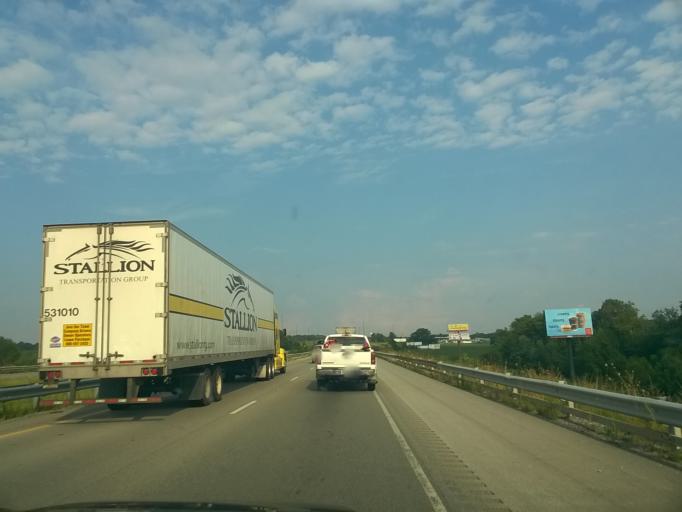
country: US
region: Indiana
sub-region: Putnam County
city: Cloverdale
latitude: 39.5327
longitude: -86.8145
